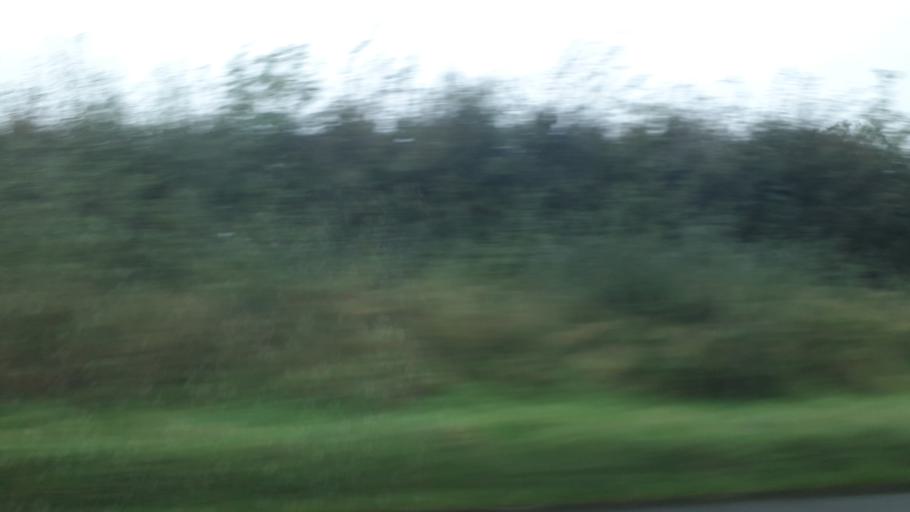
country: IE
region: Leinster
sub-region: An Longfort
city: Granard
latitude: 53.6454
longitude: -7.5041
